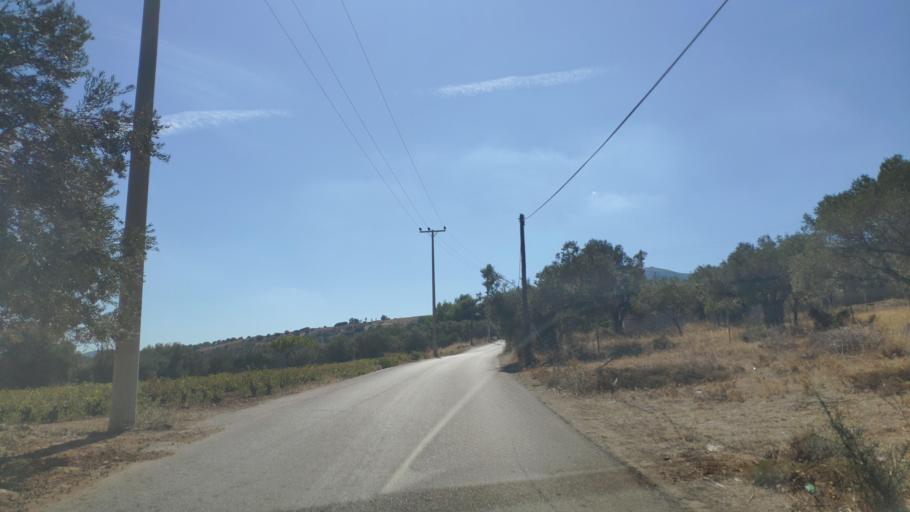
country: GR
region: Attica
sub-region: Nomarchia Anatolikis Attikis
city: Keratea
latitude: 37.8192
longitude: 23.9919
